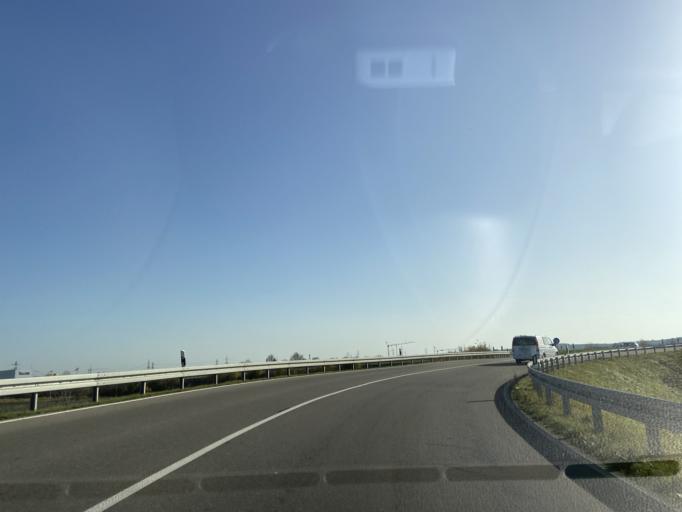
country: DE
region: Baden-Wuerttemberg
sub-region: Tuebingen Region
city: Herbertingen
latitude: 48.0676
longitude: 9.4072
